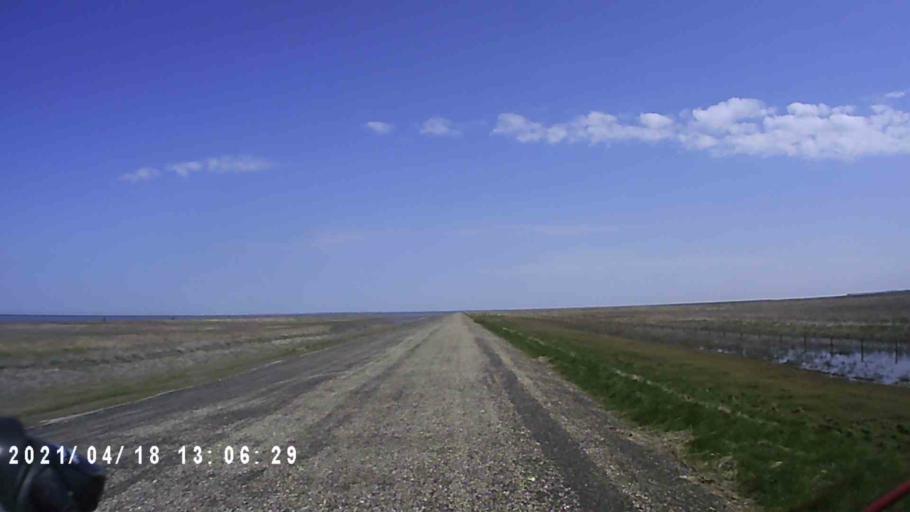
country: NL
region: Friesland
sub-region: Gemeente Dongeradeel
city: Anjum
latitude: 53.4053
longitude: 6.0895
